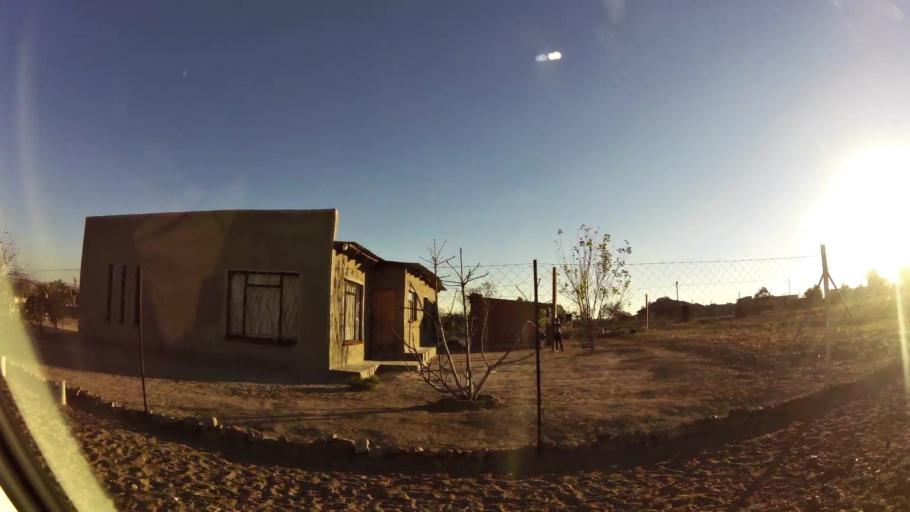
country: ZA
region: Limpopo
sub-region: Capricorn District Municipality
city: Polokwane
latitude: -23.8240
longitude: 29.3787
